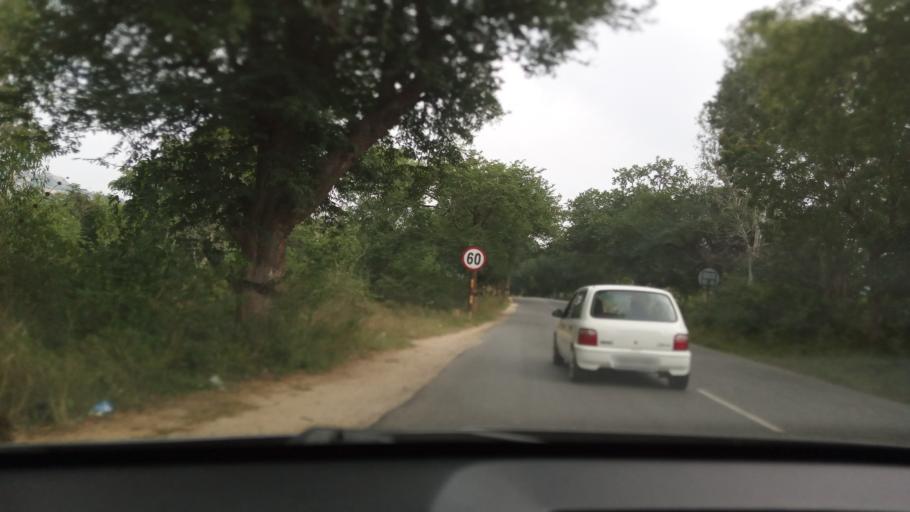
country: IN
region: Andhra Pradesh
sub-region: Chittoor
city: Pakala
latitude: 13.6564
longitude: 78.8459
